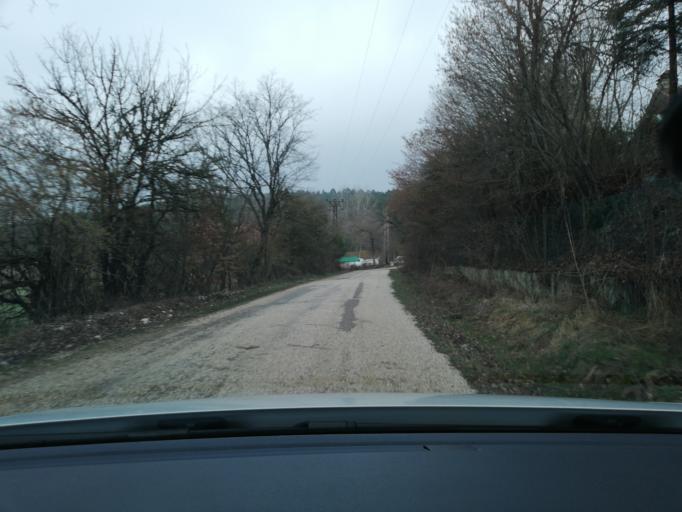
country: TR
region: Bolu
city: Bolu
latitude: 40.6833
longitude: 31.4699
